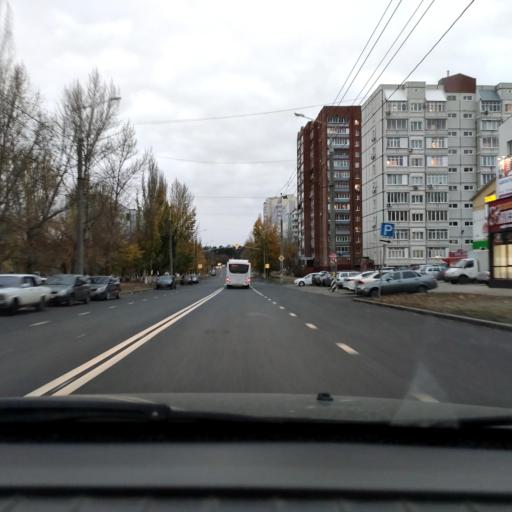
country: RU
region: Samara
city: Zhigulevsk
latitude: 53.4798
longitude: 49.4591
